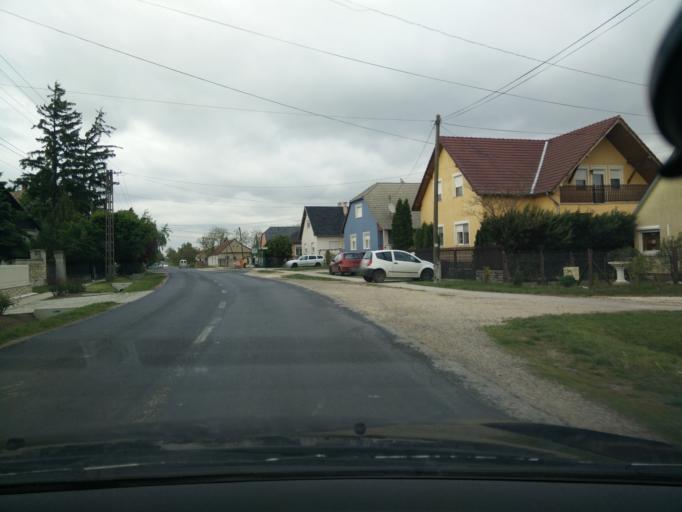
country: HU
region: Veszprem
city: Papa
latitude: 47.2871
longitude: 17.4270
